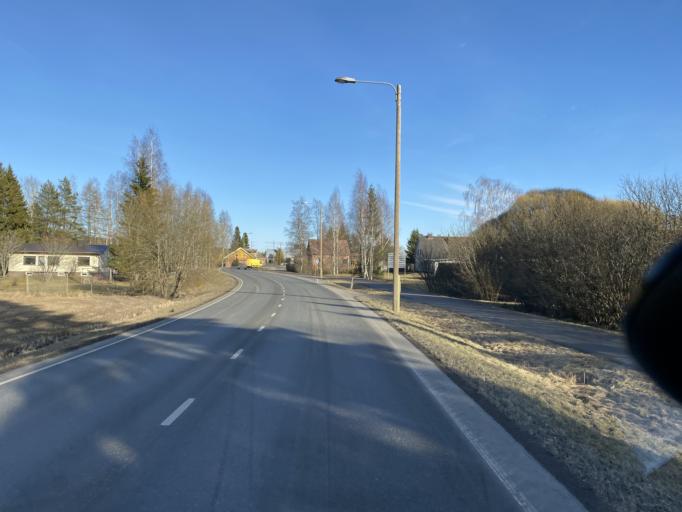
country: FI
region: Satakunta
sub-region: Pori
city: Huittinen
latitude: 61.1800
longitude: 22.7338
